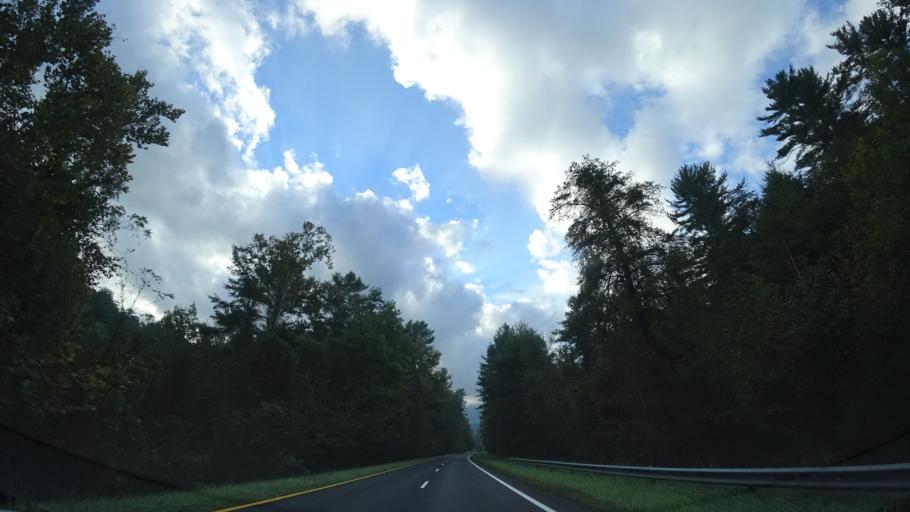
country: US
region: Virginia
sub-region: Page County
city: Luray
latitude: 38.6661
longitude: -78.3763
